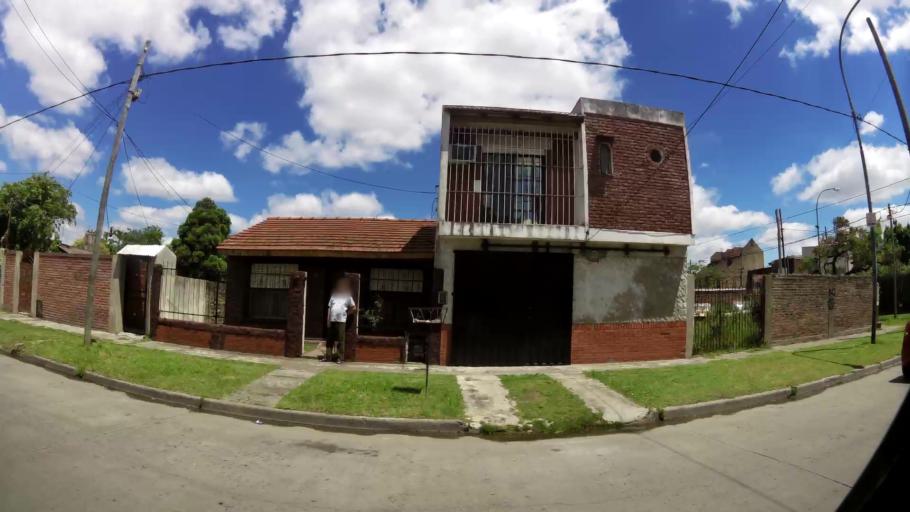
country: AR
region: Buenos Aires
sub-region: Partido de Lanus
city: Lanus
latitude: -34.7068
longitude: -58.4282
